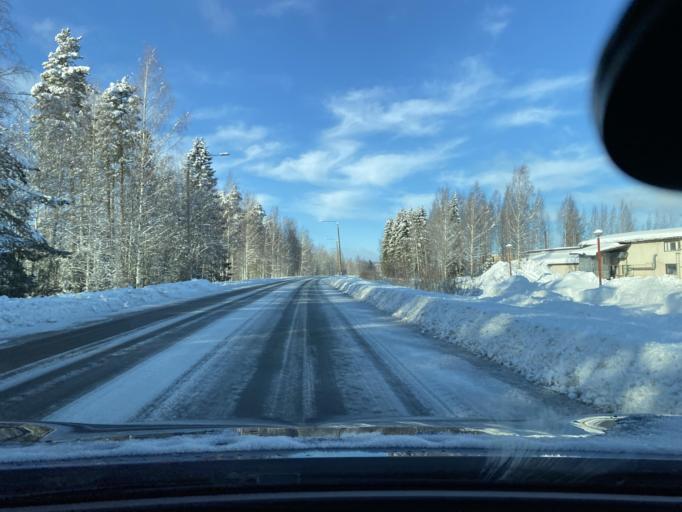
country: FI
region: Southern Savonia
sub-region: Mikkeli
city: Kangasniemi
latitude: 62.0051
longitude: 26.6484
